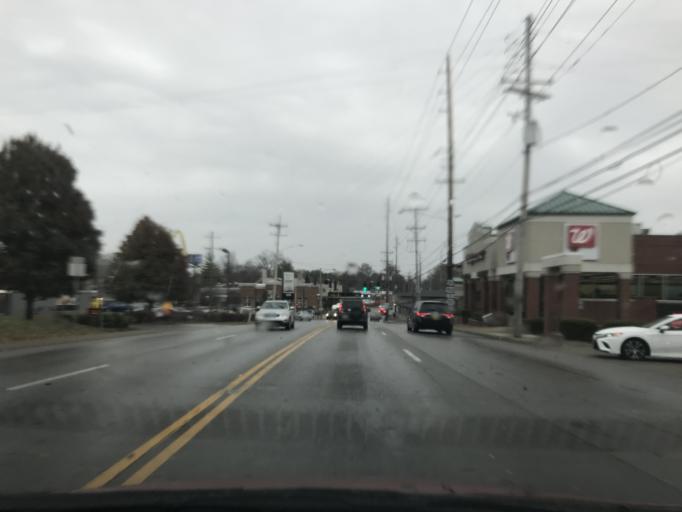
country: US
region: Kentucky
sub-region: Jefferson County
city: West Buechel
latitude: 38.2233
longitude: -85.6857
